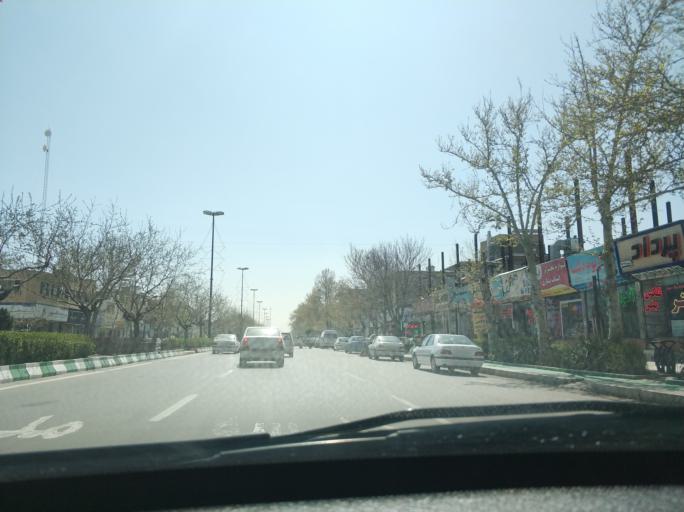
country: IR
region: Razavi Khorasan
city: Mashhad
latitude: 36.2605
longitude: 59.6061
